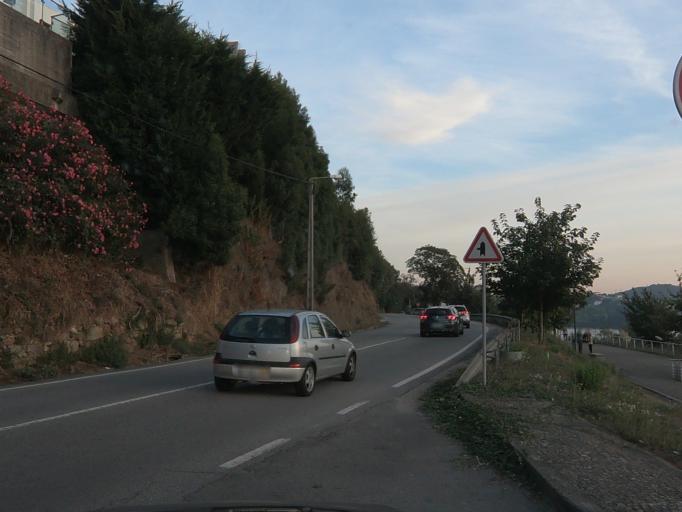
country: PT
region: Porto
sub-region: Gondomar
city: Valbom
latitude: 41.1328
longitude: -8.5694
